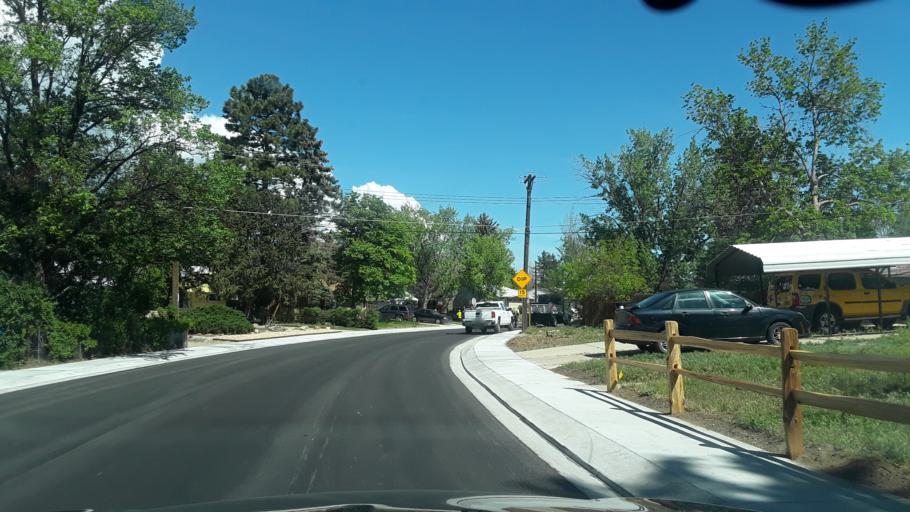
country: US
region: Colorado
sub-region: El Paso County
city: Colorado Springs
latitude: 38.8943
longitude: -104.8152
